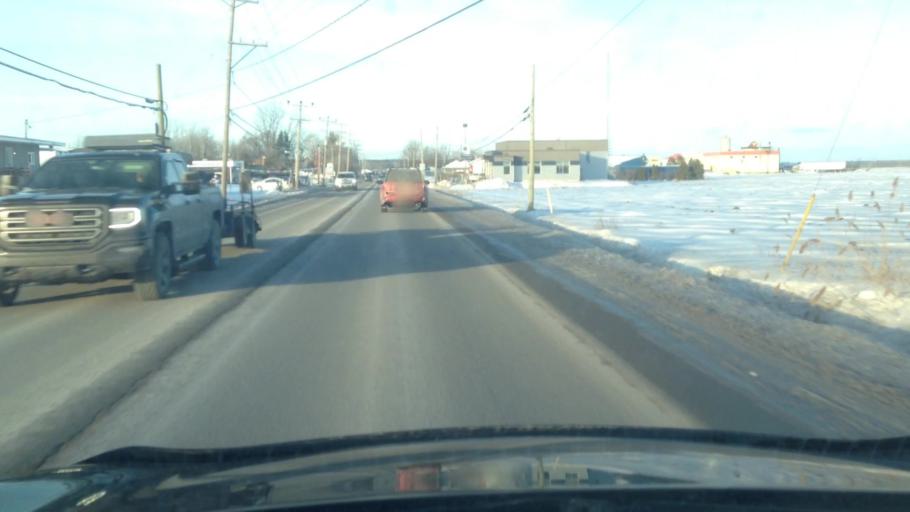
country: CA
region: Quebec
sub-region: Lanaudiere
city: Saint-Lin-Laurentides
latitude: 45.8836
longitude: -73.7577
